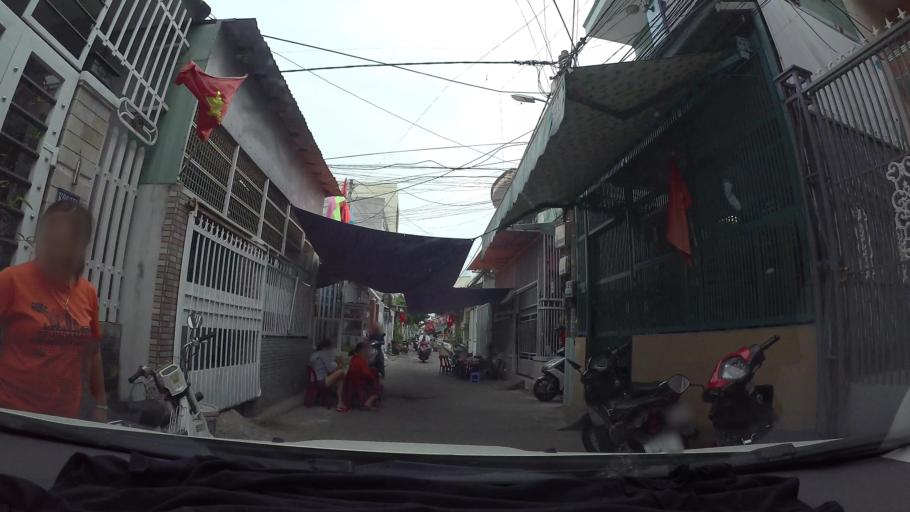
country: VN
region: Da Nang
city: Thanh Khe
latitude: 16.0675
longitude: 108.1959
